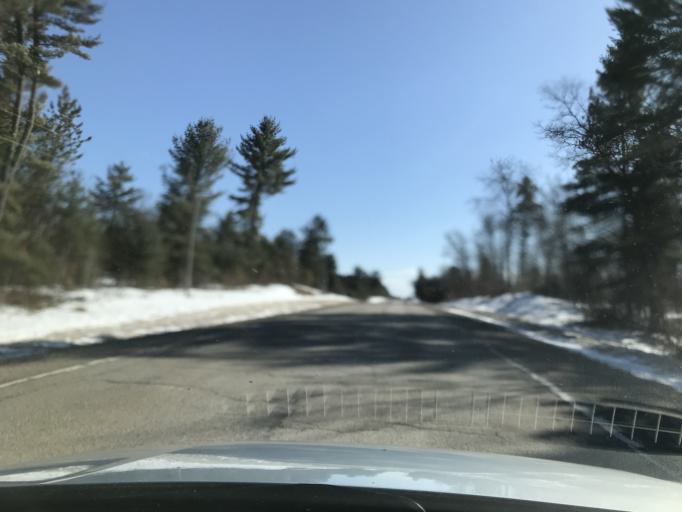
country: US
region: Wisconsin
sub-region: Marinette County
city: Niagara
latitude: 45.3889
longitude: -88.0997
